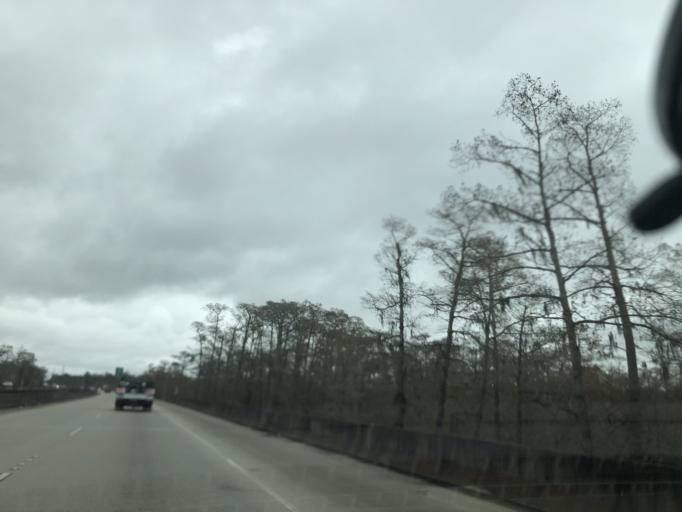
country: US
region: Louisiana
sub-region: Saint Charles Parish
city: Saint Rose
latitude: 29.9666
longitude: -90.3349
